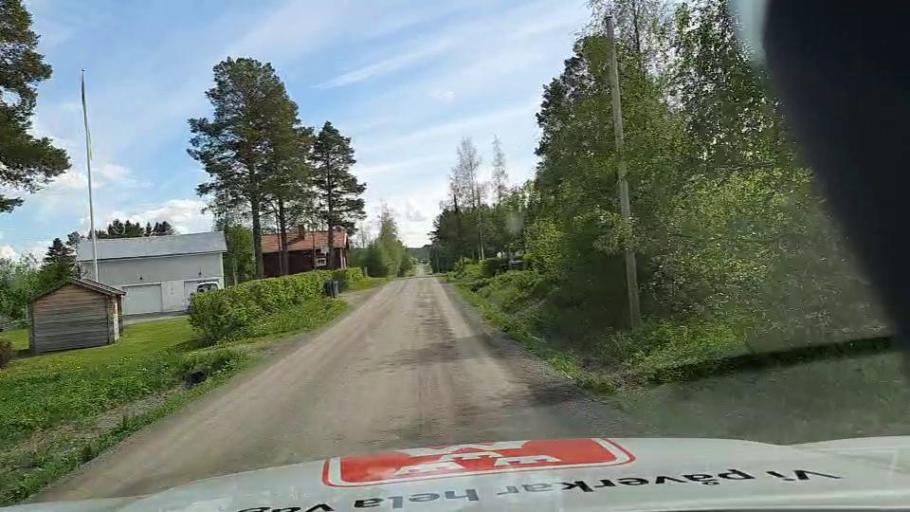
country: SE
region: Jaemtland
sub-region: OEstersunds Kommun
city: Brunflo
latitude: 62.9920
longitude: 14.8078
